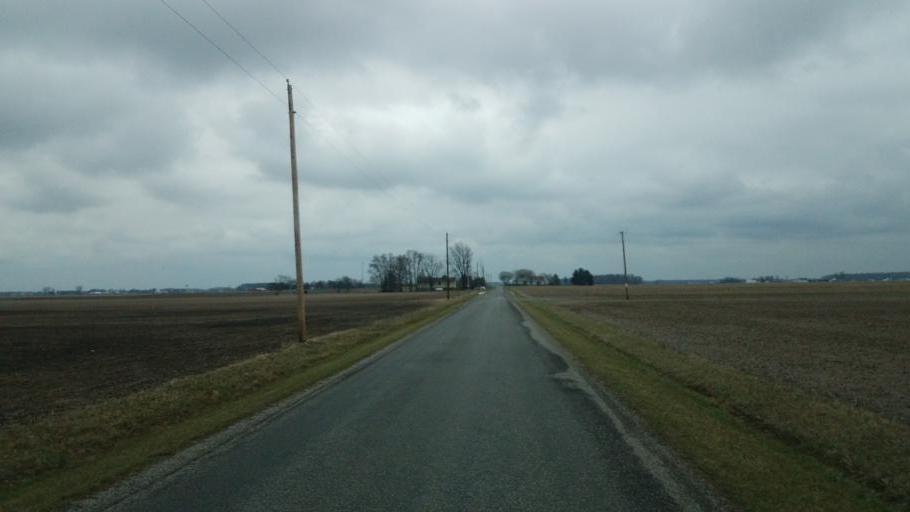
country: US
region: Ohio
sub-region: Delaware County
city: Ashley
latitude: 40.3837
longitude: -82.9874
